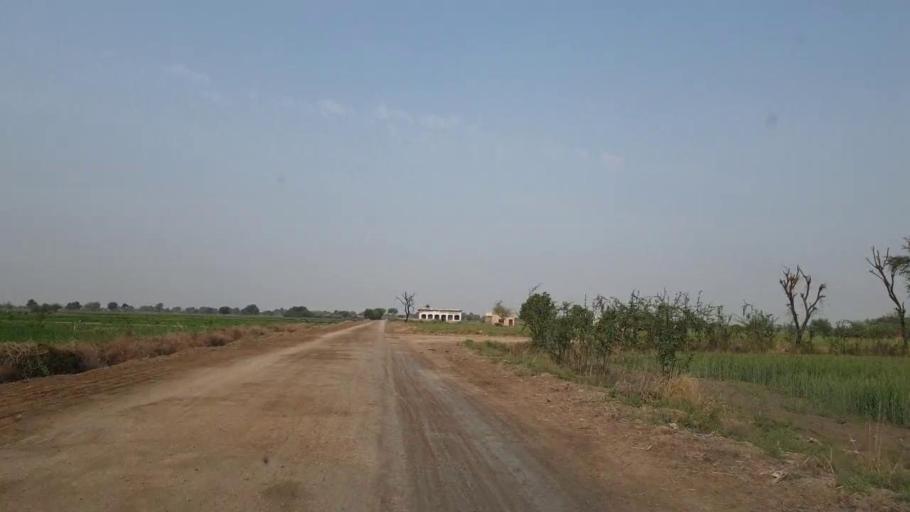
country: PK
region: Sindh
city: Mirpur Khas
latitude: 25.5638
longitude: 69.1524
